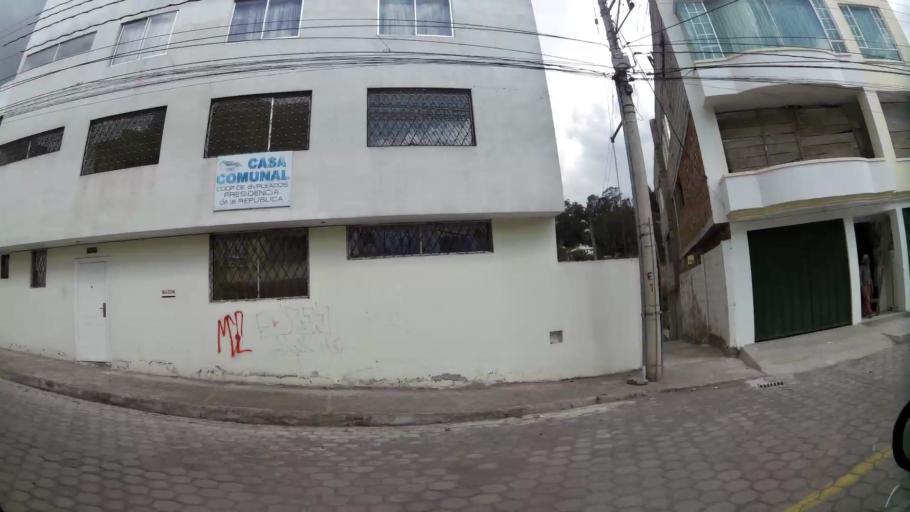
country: EC
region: Pichincha
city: Quito
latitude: -0.0920
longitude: -78.4680
